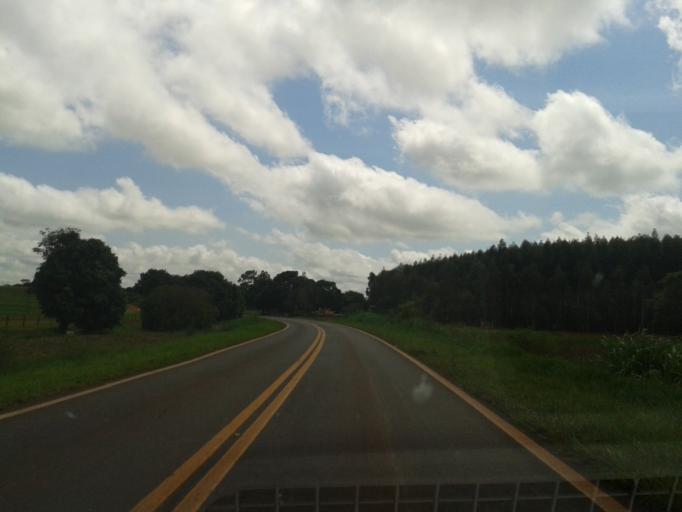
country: BR
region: Minas Gerais
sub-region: Centralina
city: Centralina
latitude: -18.7217
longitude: -49.1477
